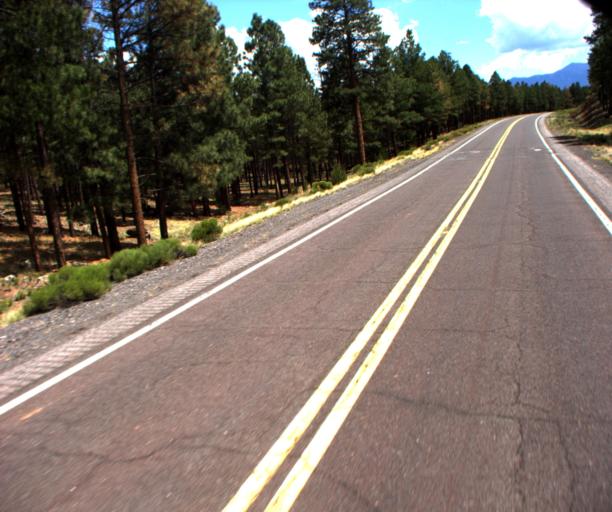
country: US
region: Arizona
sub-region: Coconino County
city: Parks
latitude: 35.5057
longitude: -111.8230
